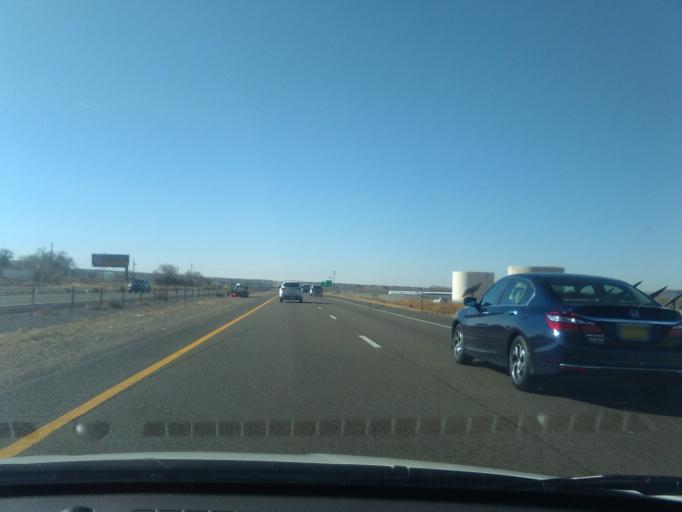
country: US
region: New Mexico
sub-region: Sandoval County
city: San Felipe Pueblo
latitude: 35.3843
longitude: -106.4623
